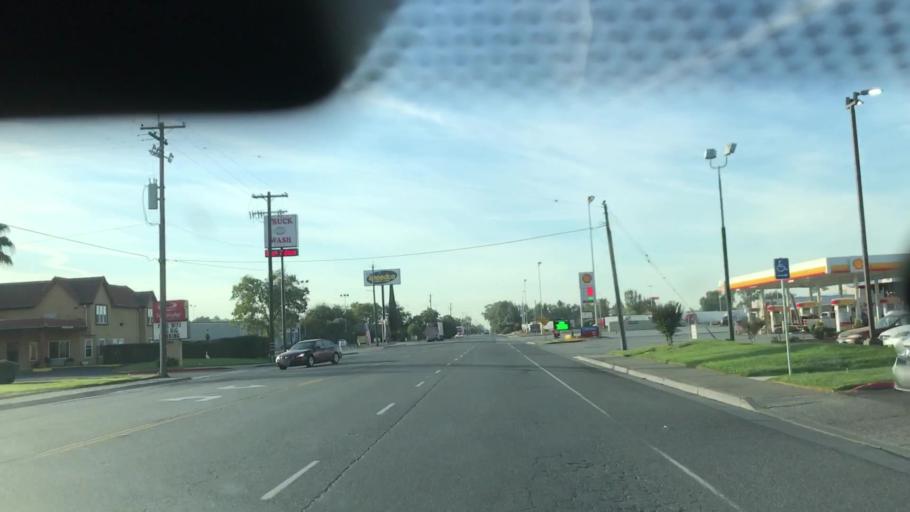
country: US
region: California
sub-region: Tehama County
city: Corning
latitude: 39.9051
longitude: -122.1976
